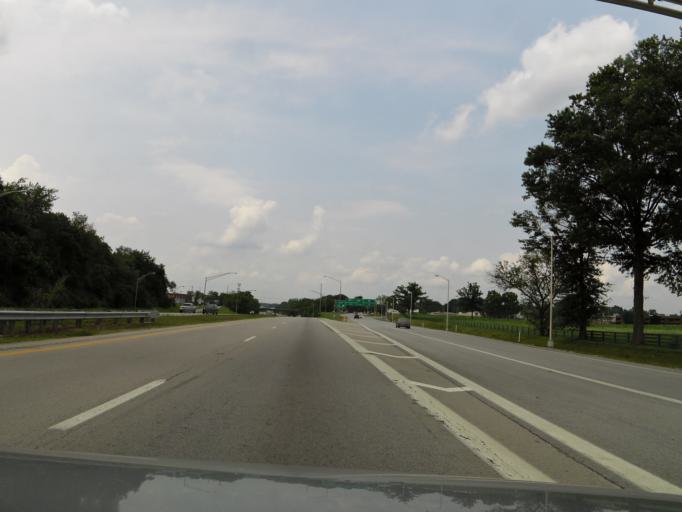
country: US
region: Kentucky
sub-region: Jefferson County
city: Windy Hills
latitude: 38.2764
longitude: -85.6327
